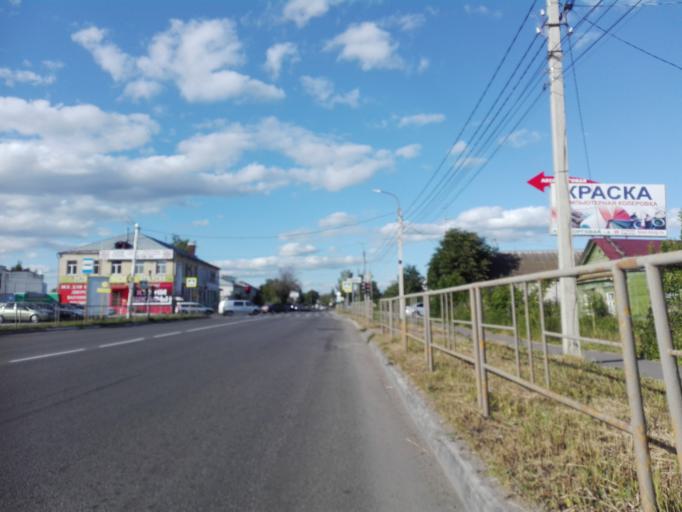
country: RU
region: Orjol
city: Orel
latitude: 52.9421
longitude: 36.0720
